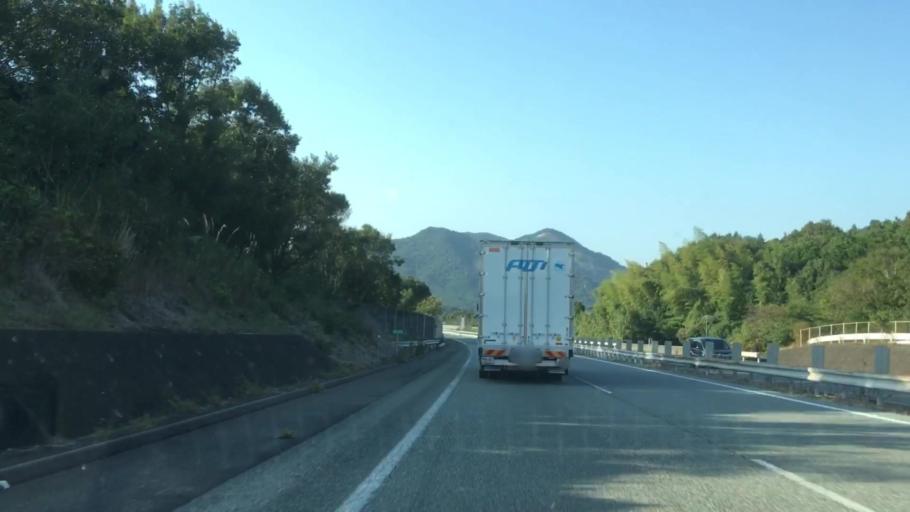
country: JP
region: Yamaguchi
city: Hofu
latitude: 34.0652
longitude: 131.5011
